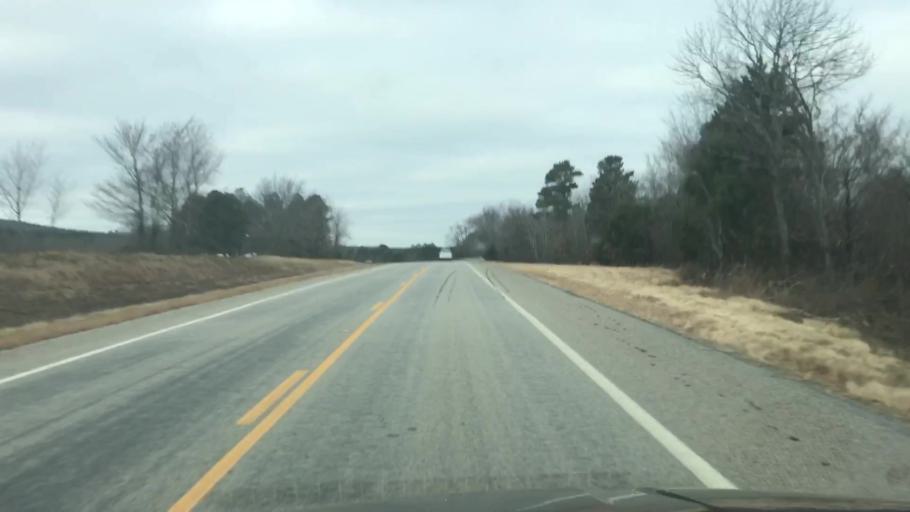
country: US
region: Arkansas
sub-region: Scott County
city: Waldron
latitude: 34.7024
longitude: -93.9193
